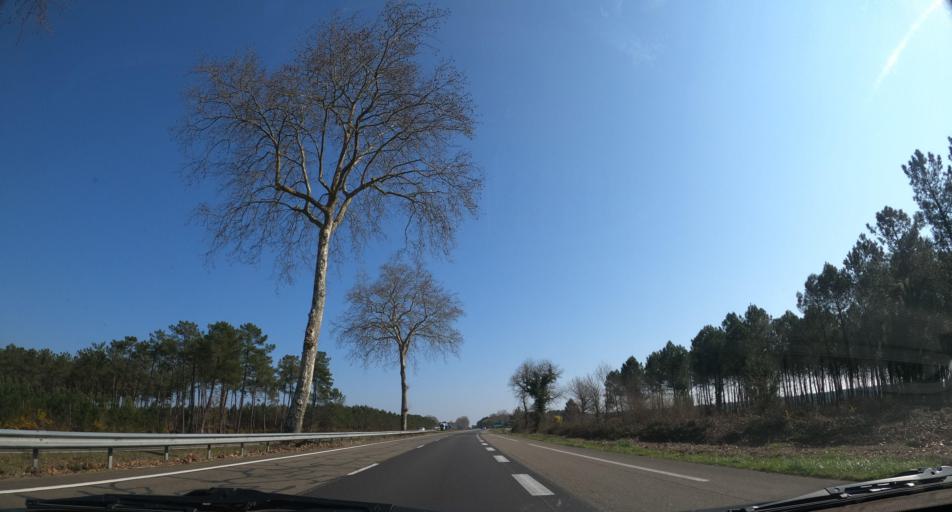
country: FR
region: Aquitaine
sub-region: Departement des Landes
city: Riviere-Saas-et-Gourby
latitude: 43.7091
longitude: -1.1599
